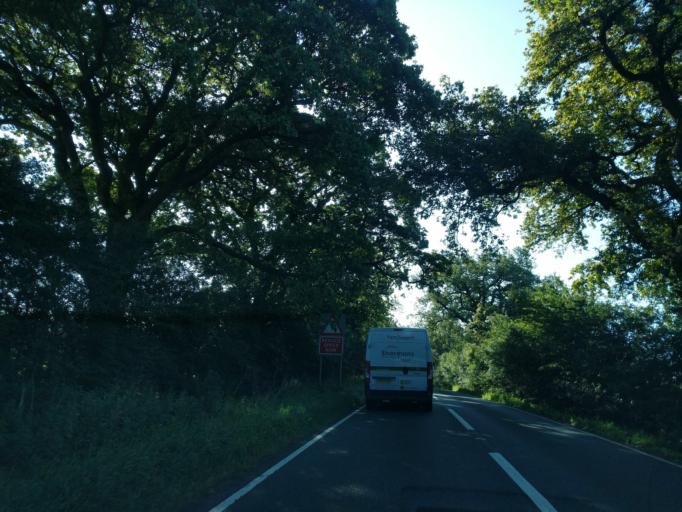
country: GB
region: England
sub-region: Lincolnshire
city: Bourne
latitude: 52.8001
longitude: -0.4712
